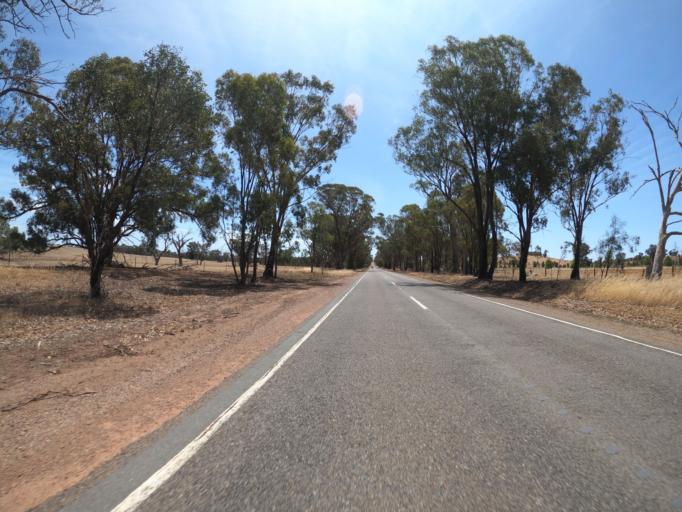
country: AU
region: Victoria
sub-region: Benalla
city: Benalla
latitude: -36.3590
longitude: 145.9667
